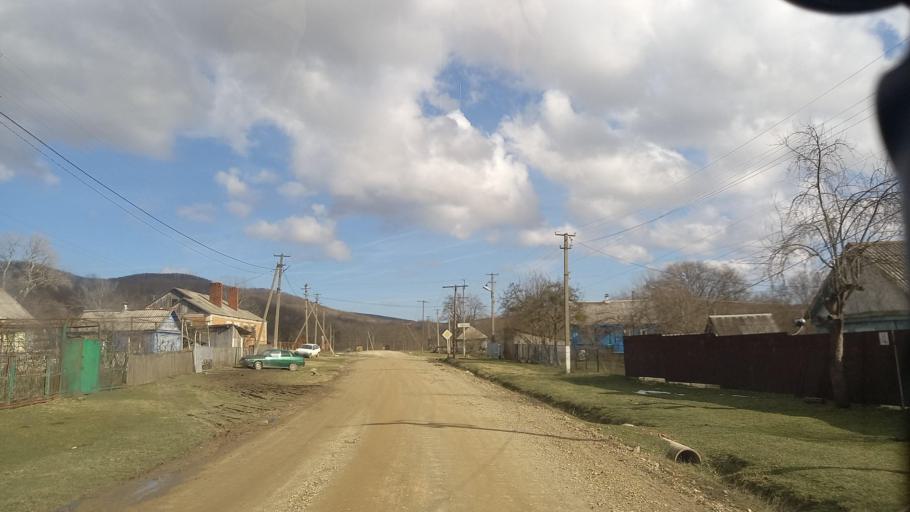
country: RU
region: Krasnodarskiy
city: Smolenskaya
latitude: 44.6026
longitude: 38.8594
